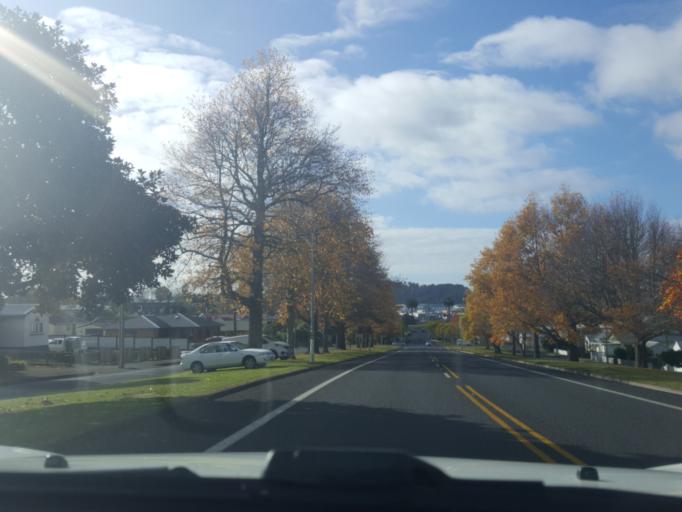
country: NZ
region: Waikato
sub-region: Hauraki District
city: Waihi
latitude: -37.3922
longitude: 175.8337
